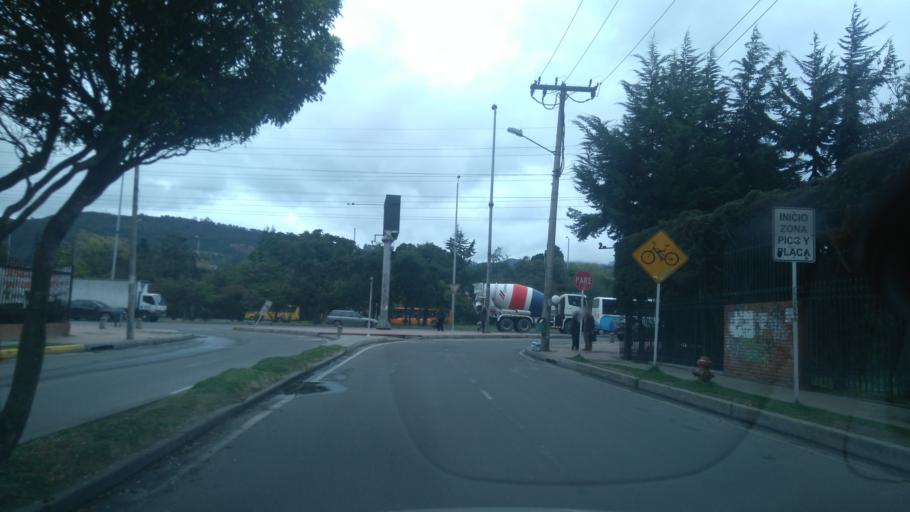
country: CO
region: Cundinamarca
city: Cota
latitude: 4.7651
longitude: -74.0451
